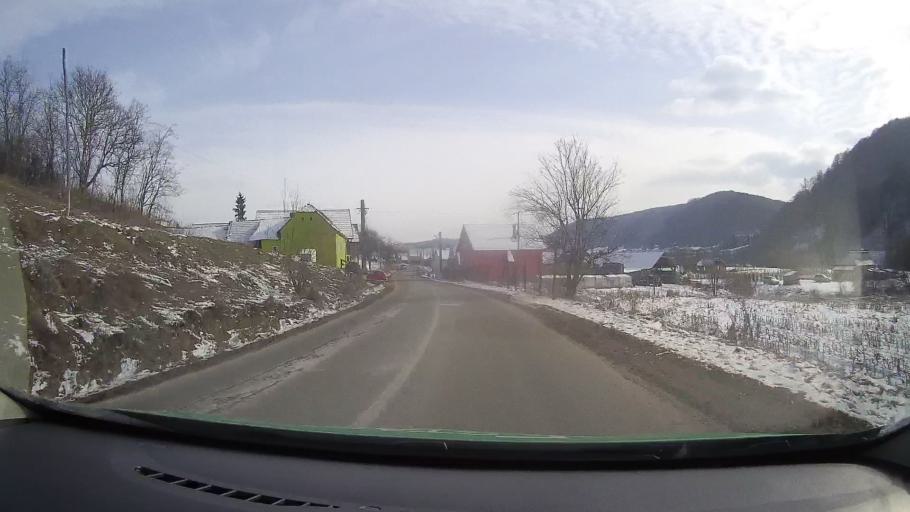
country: RO
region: Mures
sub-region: Comuna Apold
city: Saes
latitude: 46.1611
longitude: 24.7619
